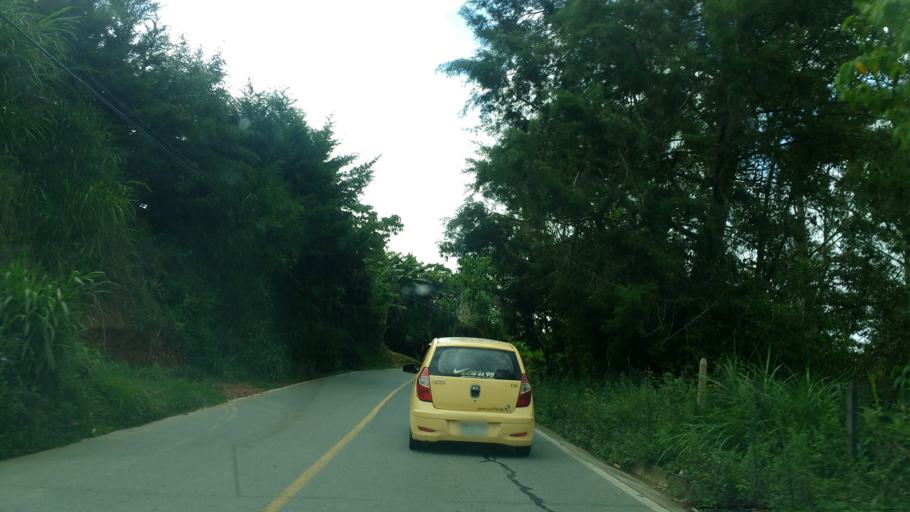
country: CO
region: Antioquia
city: Marinilla
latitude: 6.1828
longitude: -75.3045
